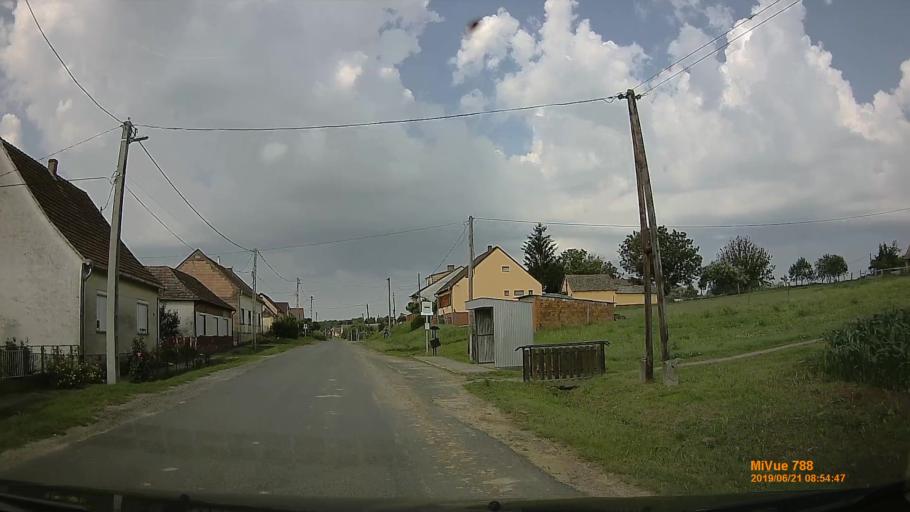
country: HU
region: Baranya
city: Buekkoesd
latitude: 46.1631
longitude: 17.8828
